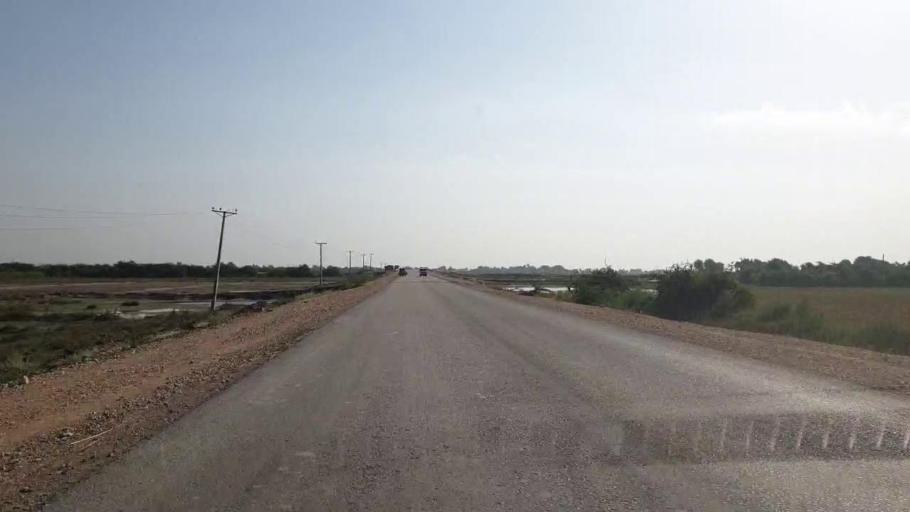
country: PK
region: Sindh
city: Tando Bago
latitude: 24.6570
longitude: 69.0164
